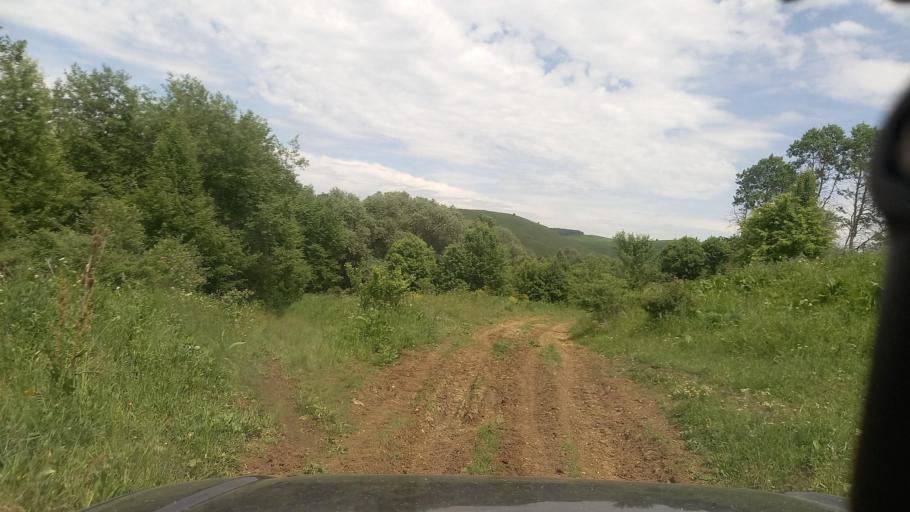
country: RU
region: Karachayevo-Cherkesiya
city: Pregradnaya
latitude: 44.0777
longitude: 41.2668
